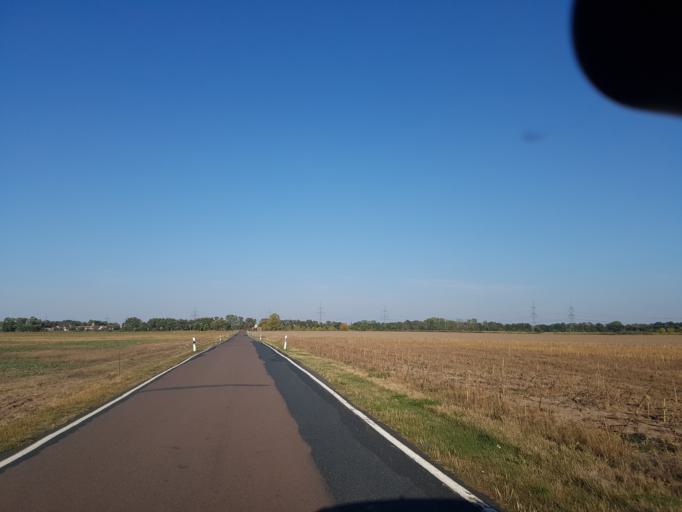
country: DE
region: Saxony
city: Nauwalde
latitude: 51.4099
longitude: 13.3810
